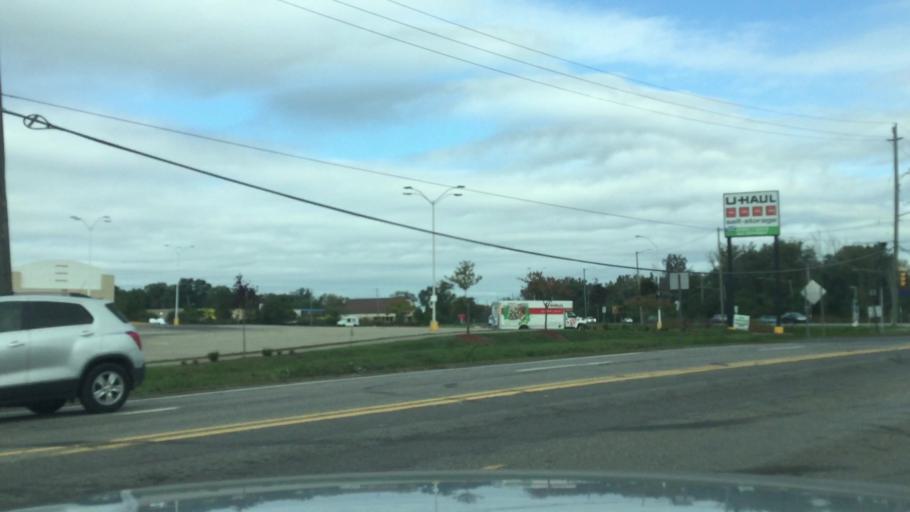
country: US
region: Michigan
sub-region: Oakland County
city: Keego Harbor
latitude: 42.6411
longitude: -83.3555
